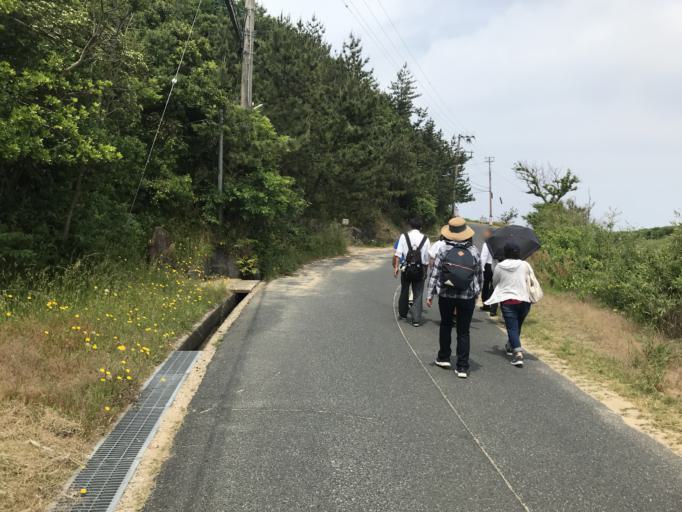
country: JP
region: Kyoto
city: Miyazu
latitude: 35.7012
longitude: 135.0520
